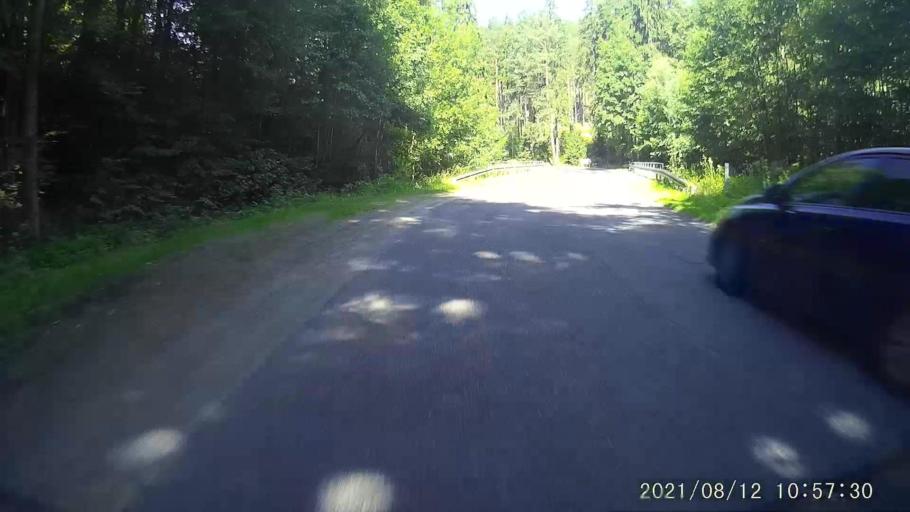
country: PL
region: Lower Silesian Voivodeship
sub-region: Powiat klodzki
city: Polanica-Zdroj
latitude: 50.3982
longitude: 16.4956
